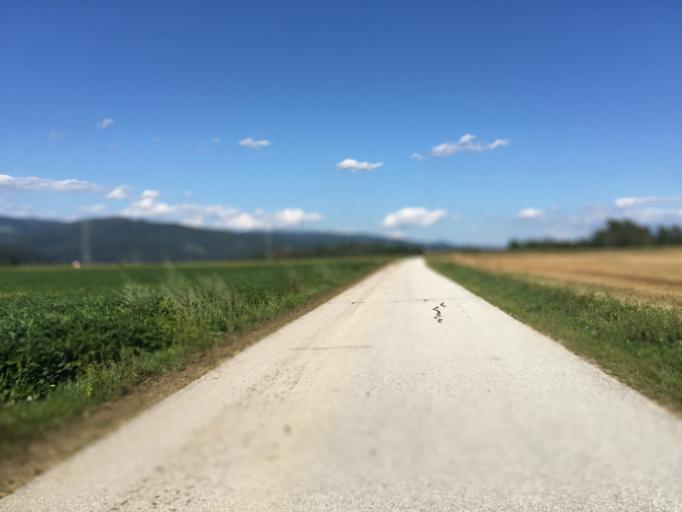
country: AT
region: Carinthia
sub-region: Politischer Bezirk Volkermarkt
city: Feistritz ob Bleiburg
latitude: 46.5655
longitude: 14.7598
